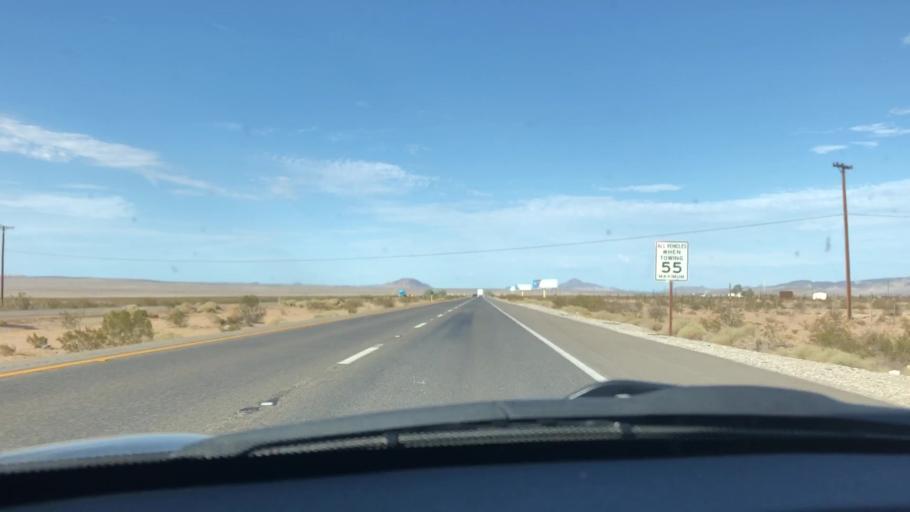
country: US
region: California
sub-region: San Bernardino County
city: Fort Irwin
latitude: 34.9746
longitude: -116.6191
